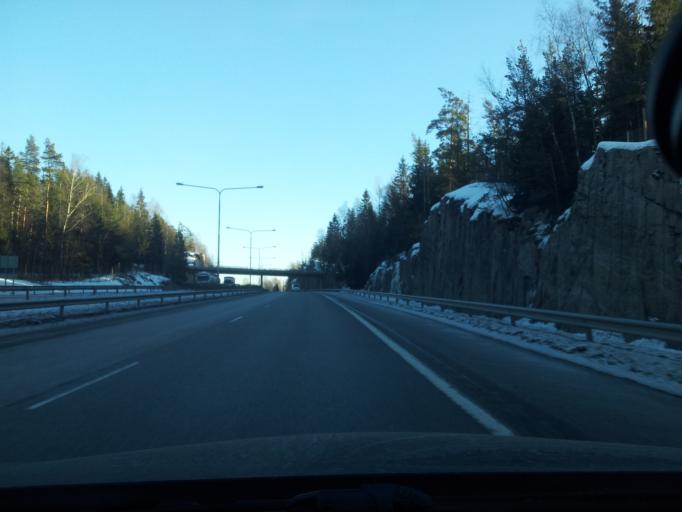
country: FI
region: Uusimaa
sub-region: Helsinki
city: Espoo
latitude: 60.2302
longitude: 24.5905
